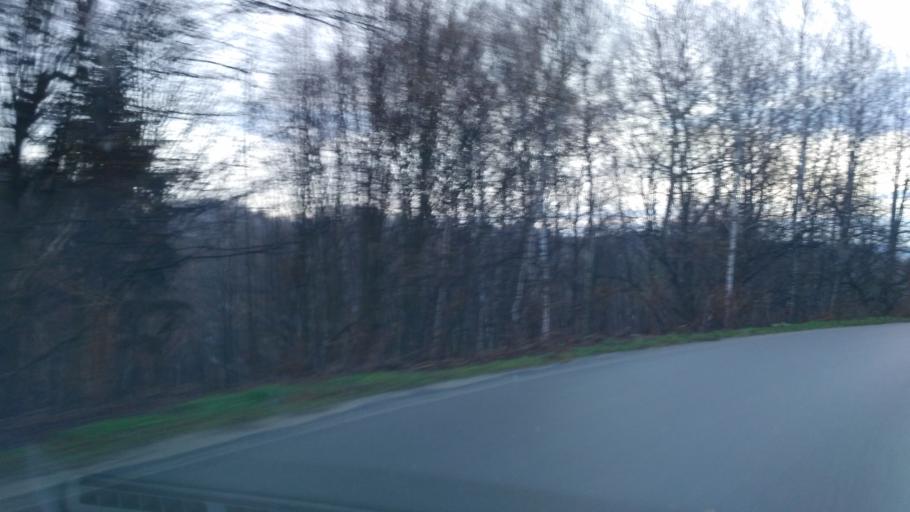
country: PL
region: Subcarpathian Voivodeship
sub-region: Powiat strzyzowski
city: Jawornik
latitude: 49.8725
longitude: 21.8724
